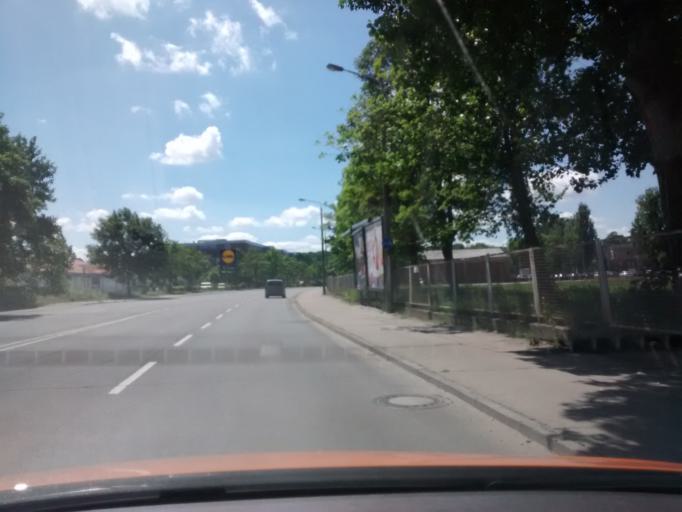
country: DE
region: Brandenburg
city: Potsdam
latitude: 52.3800
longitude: 13.0867
